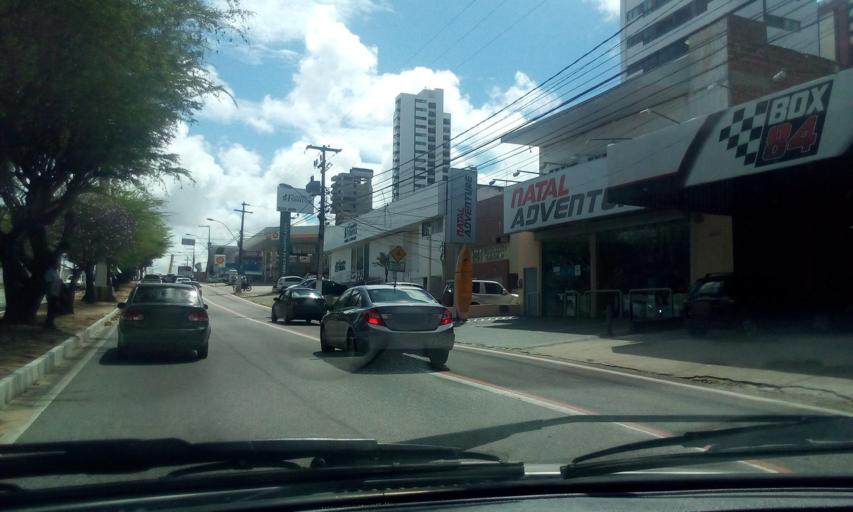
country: BR
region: Rio Grande do Norte
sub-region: Natal
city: Natal
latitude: -5.8202
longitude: -35.2132
